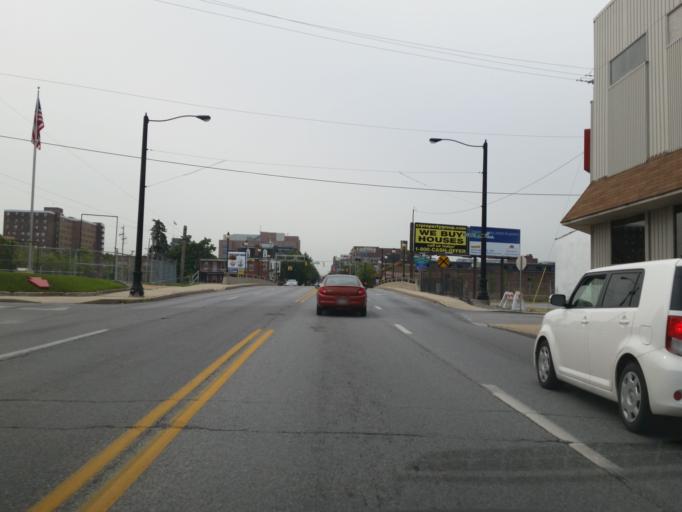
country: US
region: Pennsylvania
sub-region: York County
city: York
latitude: 39.9688
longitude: -76.7310
